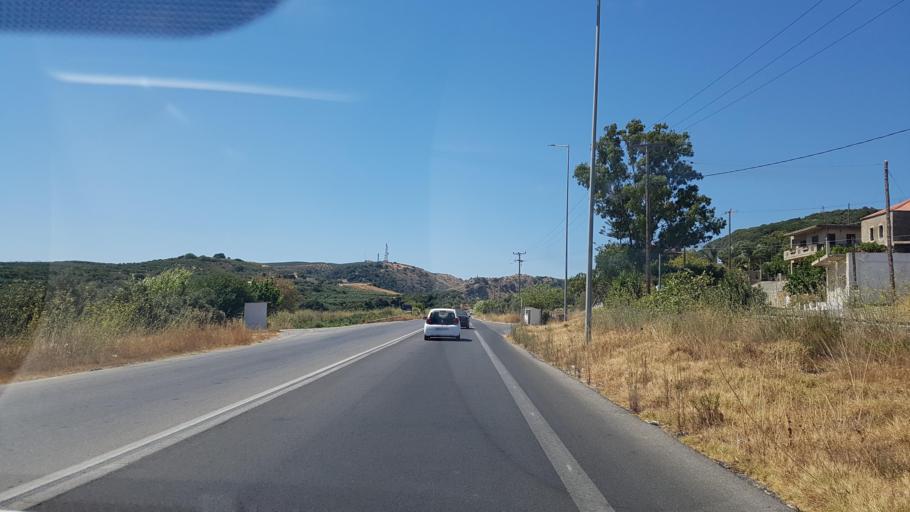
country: GR
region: Crete
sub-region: Nomos Chanias
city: Kolympari
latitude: 35.5246
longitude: 23.7475
